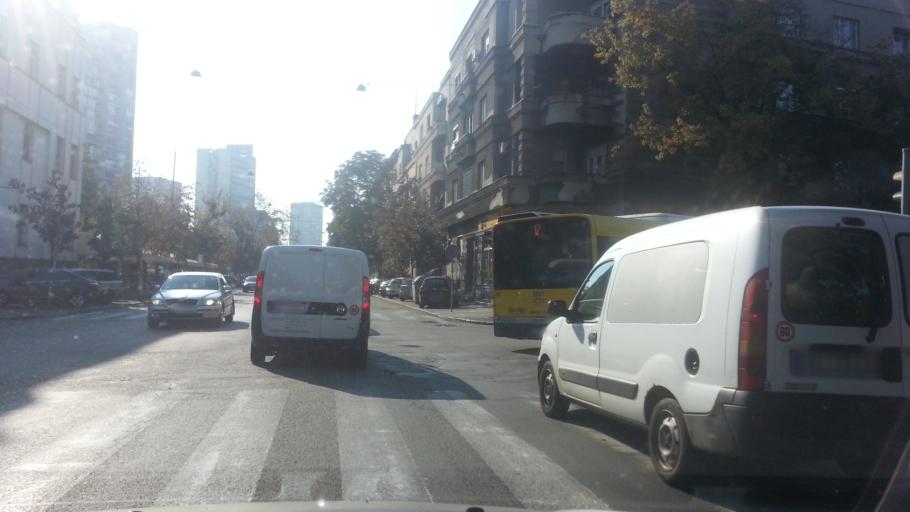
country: RS
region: Central Serbia
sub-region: Belgrade
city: Zemun
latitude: 44.8407
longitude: 20.4145
